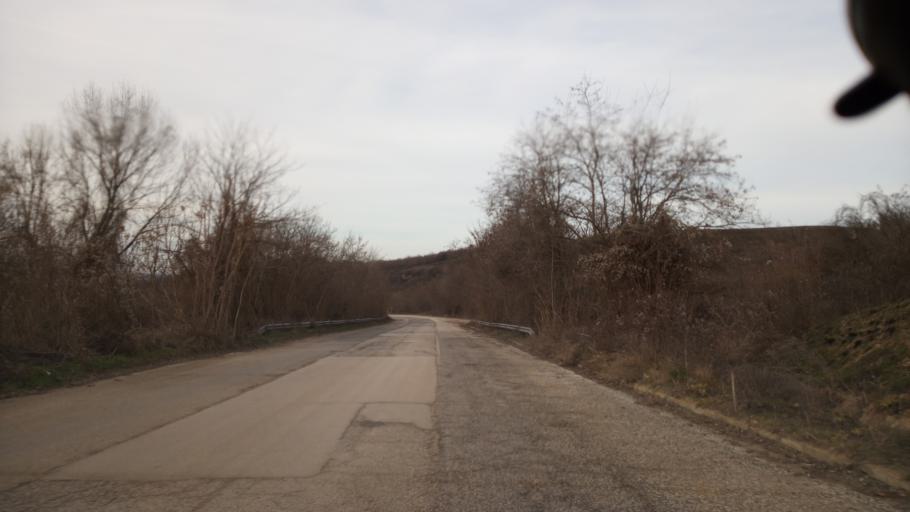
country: BG
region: Pleven
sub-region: Obshtina Nikopol
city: Nikopol
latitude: 43.5946
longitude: 24.9583
